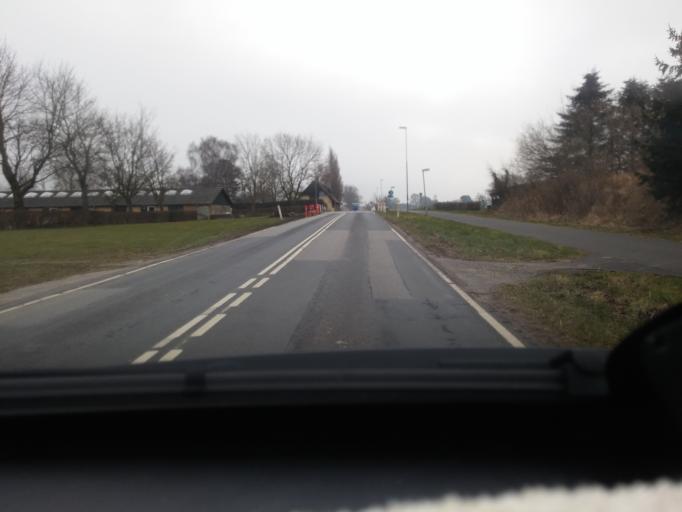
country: DK
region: South Denmark
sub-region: Nyborg Kommune
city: Ullerslev
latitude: 55.3633
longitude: 10.7264
